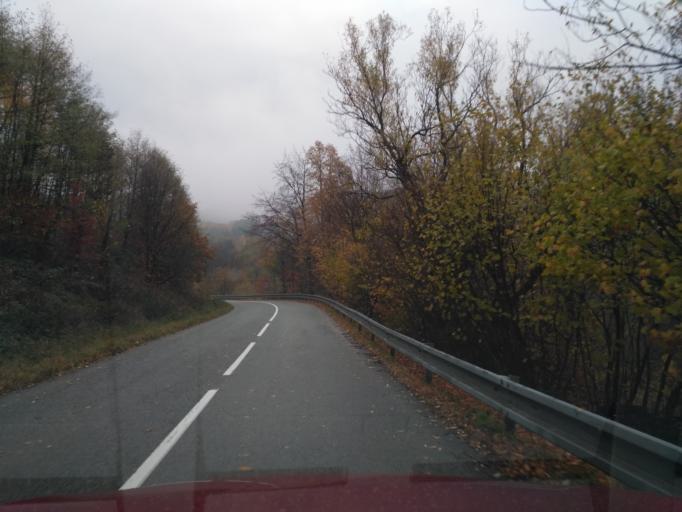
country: SK
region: Kosicky
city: Medzev
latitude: 48.7108
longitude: 20.7991
